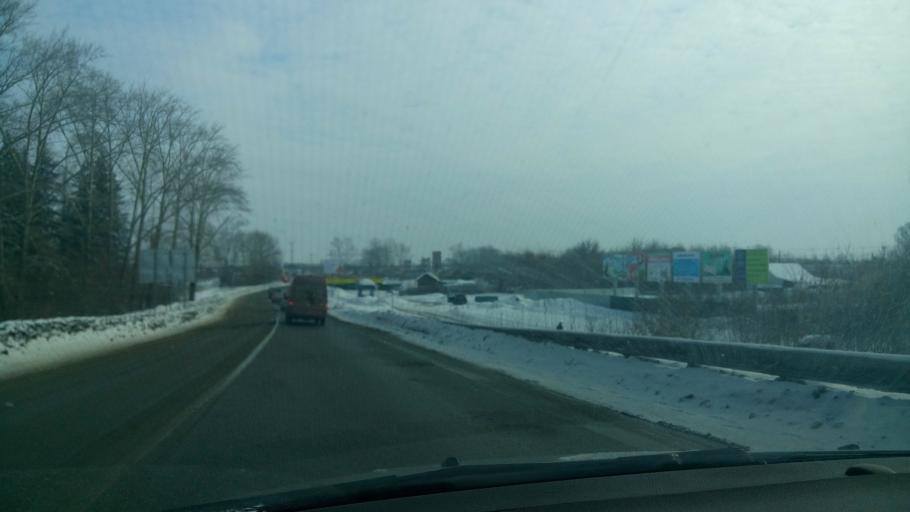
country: RU
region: Sverdlovsk
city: Bogdanovich
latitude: 56.7755
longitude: 62.0231
